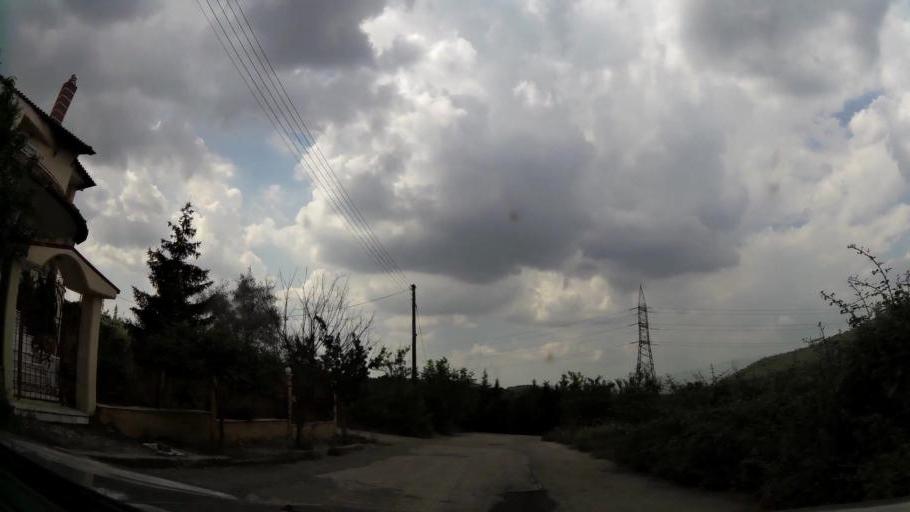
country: GR
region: West Macedonia
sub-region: Nomos Kozanis
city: Koila
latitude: 40.3308
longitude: 21.8248
